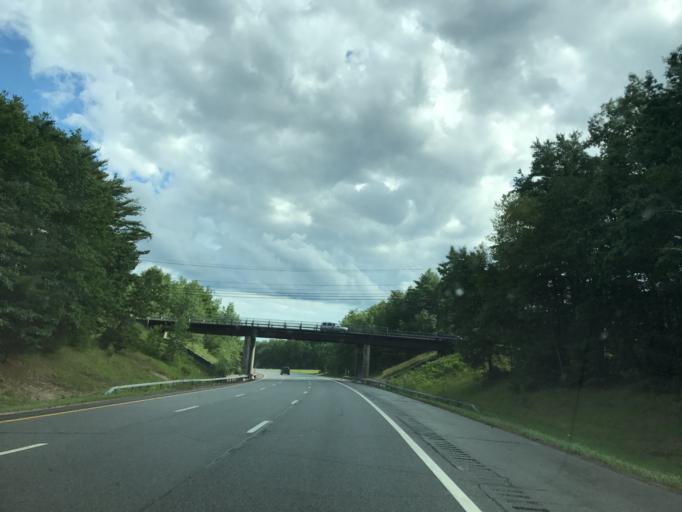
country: US
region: New York
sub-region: Warren County
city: Glens Falls North
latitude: 43.3603
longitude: -73.7045
